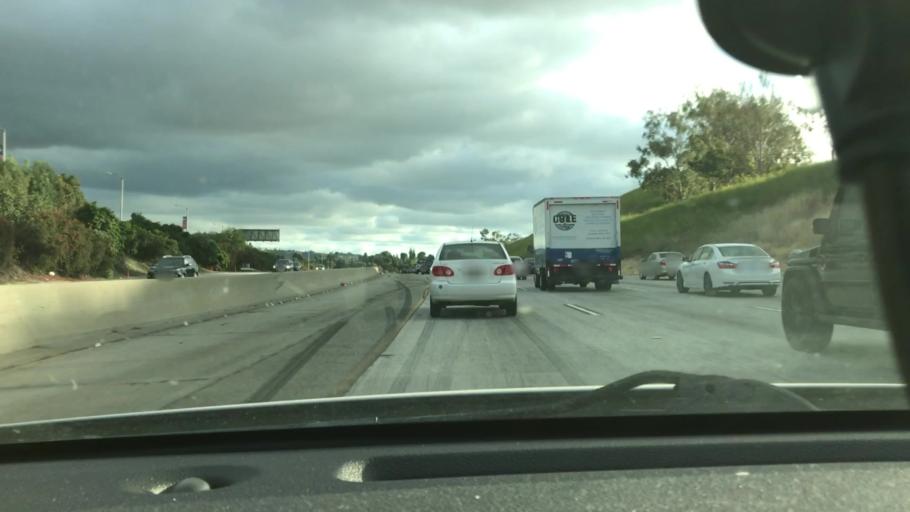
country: US
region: California
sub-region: Los Angeles County
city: Diamond Bar
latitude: 34.0364
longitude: -117.8067
